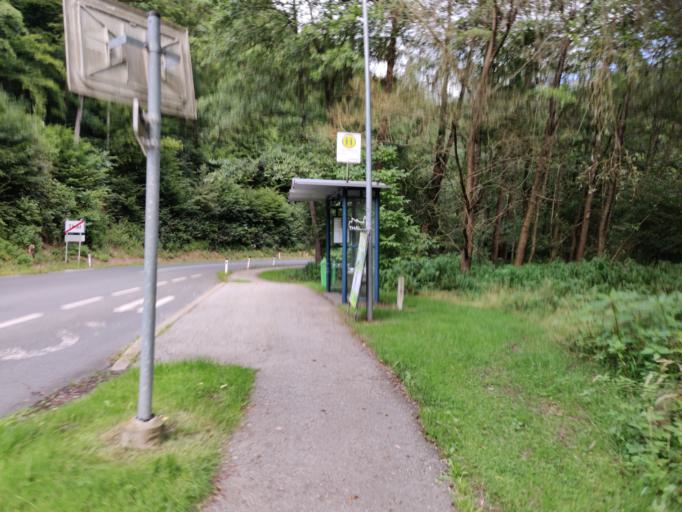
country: AT
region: Styria
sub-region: Politischer Bezirk Graz-Umgebung
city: Thal
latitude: 47.0796
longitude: 15.3614
